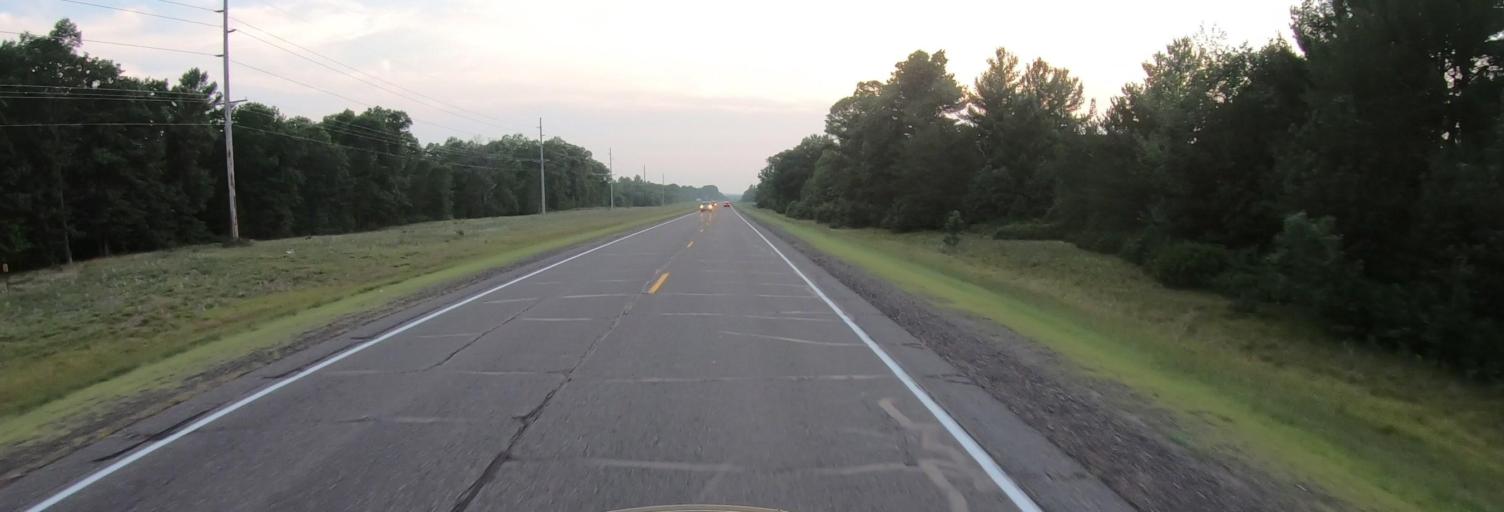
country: US
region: Wisconsin
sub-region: Burnett County
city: Grantsburg
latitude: 45.7731
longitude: -92.7500
